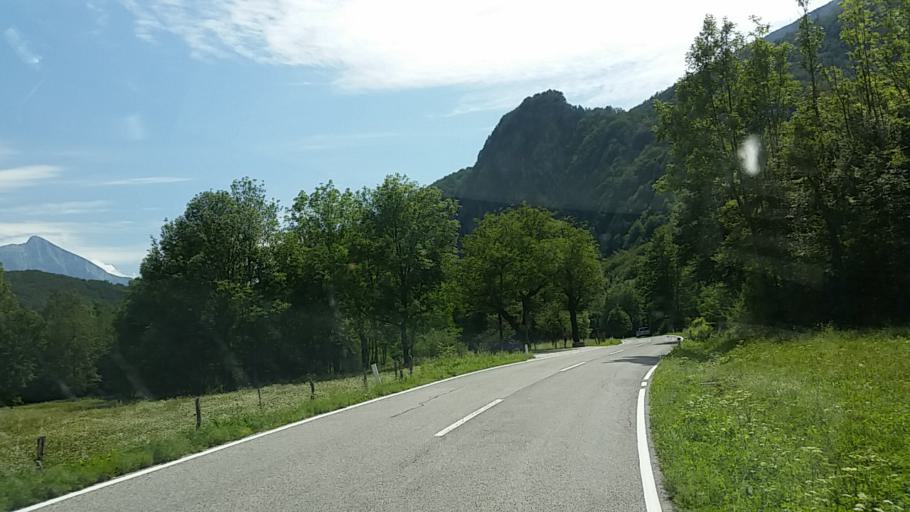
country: SI
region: Bovec
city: Bovec
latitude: 46.2858
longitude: 13.5118
